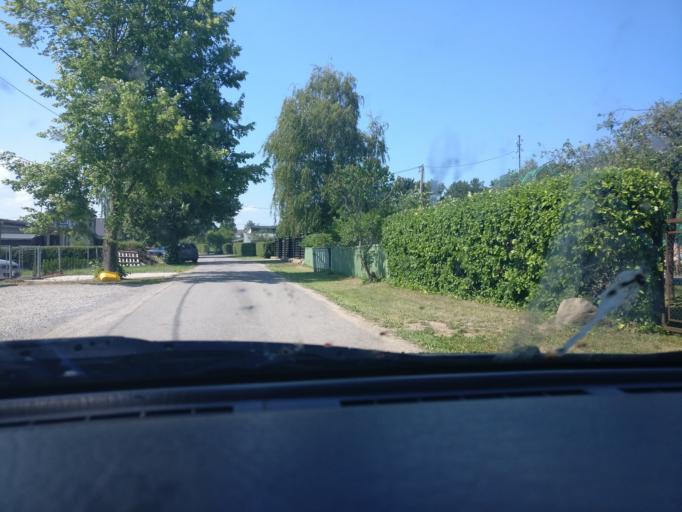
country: EE
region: Tartu
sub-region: UElenurme vald
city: Ulenurme
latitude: 58.3469
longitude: 26.7899
